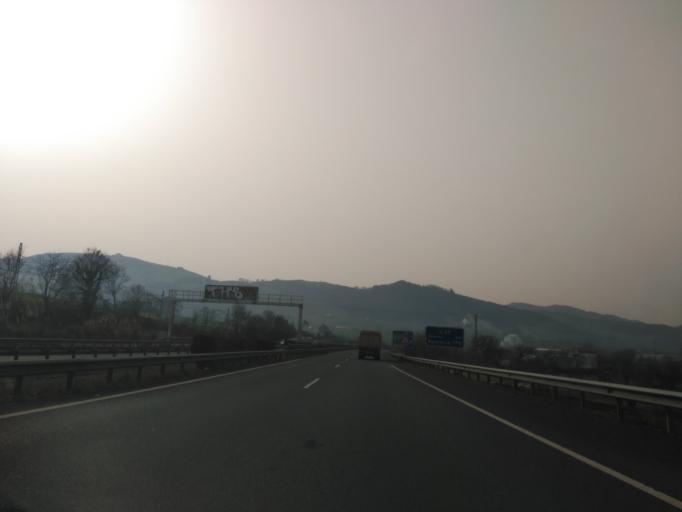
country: ES
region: Cantabria
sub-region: Provincia de Cantabria
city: Torrelavega
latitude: 43.3373
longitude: -4.0319
